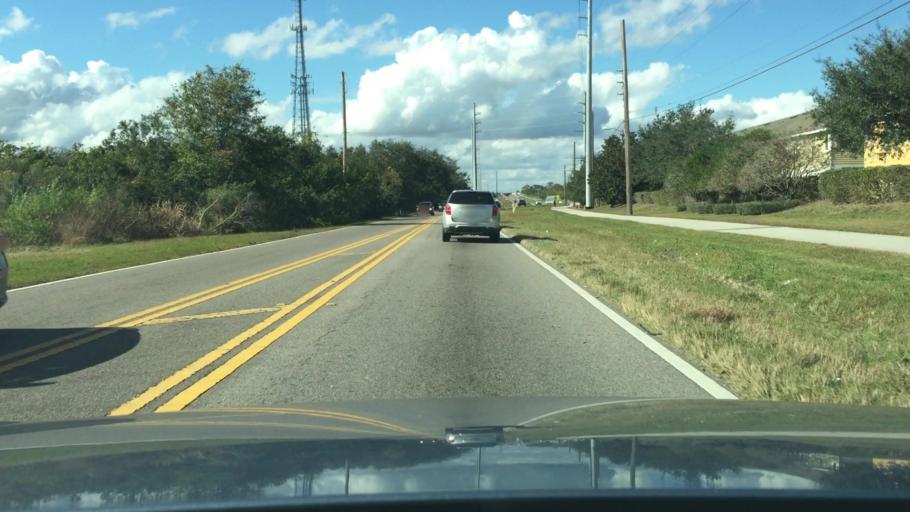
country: US
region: Florida
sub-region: Osceola County
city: Saint Cloud
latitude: 28.2519
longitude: -81.3236
